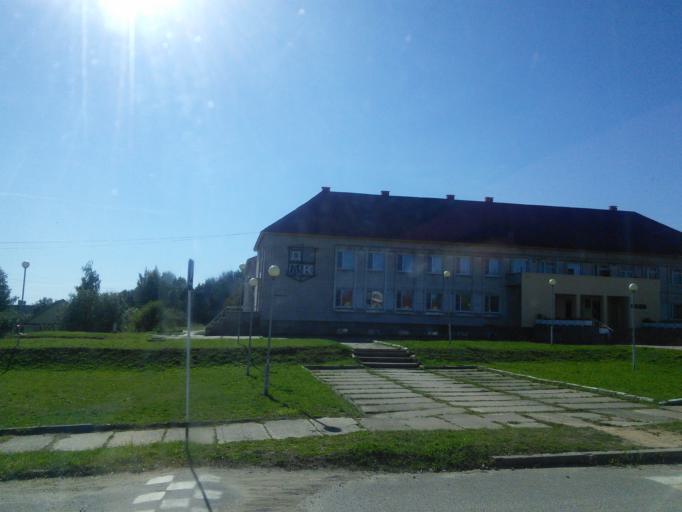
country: RU
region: Tverskaya
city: Kesova Gora
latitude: 57.5795
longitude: 37.2914
